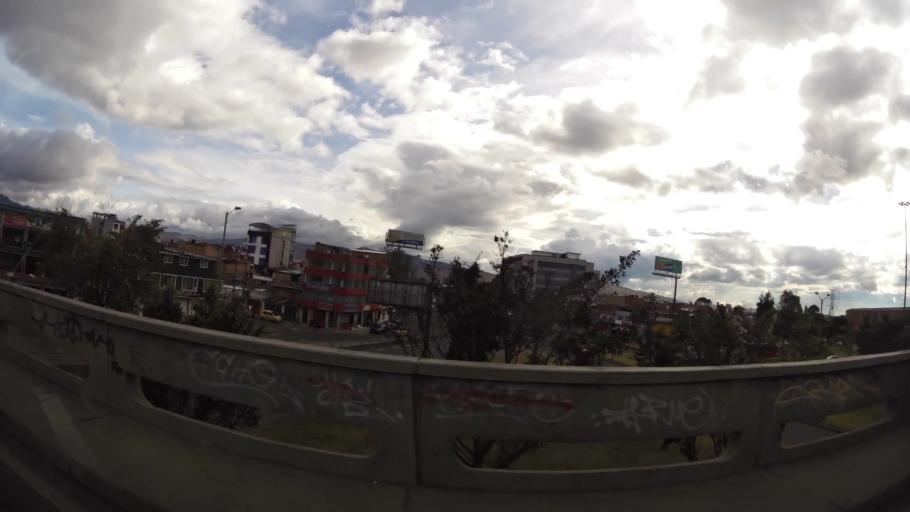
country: CO
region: Bogota D.C.
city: Bogota
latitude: 4.6092
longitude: -74.1287
